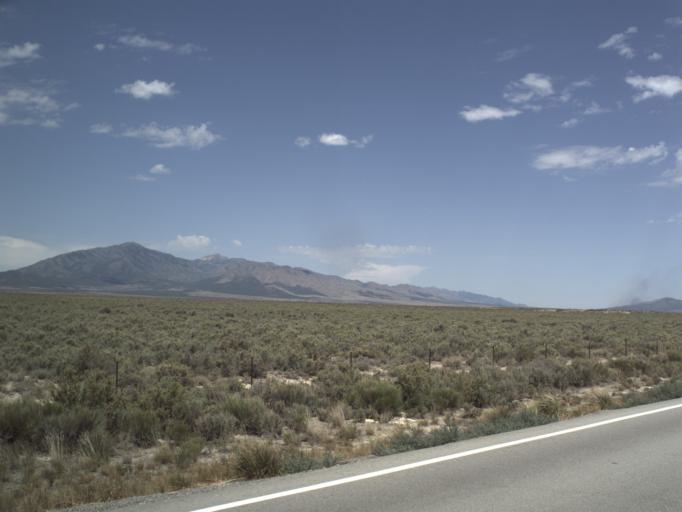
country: US
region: Utah
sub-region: Tooele County
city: Tooele
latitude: 40.2348
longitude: -112.4025
